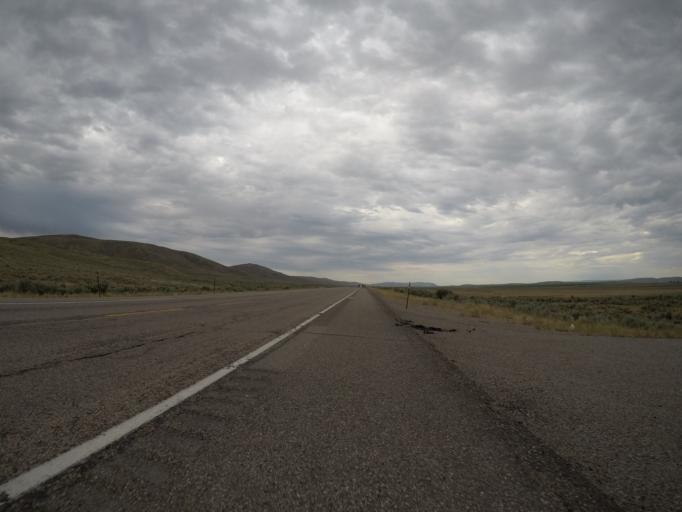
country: US
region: Utah
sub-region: Rich County
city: Randolph
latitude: 41.8749
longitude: -110.9665
